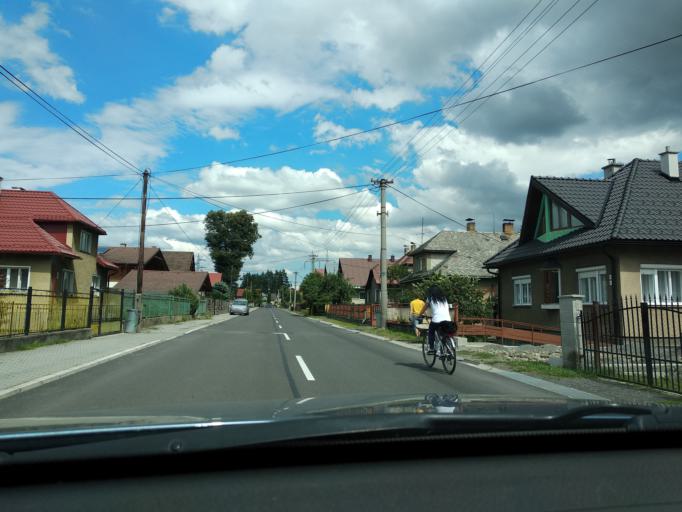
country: SK
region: Zilinsky
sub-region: Okres Zilina
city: Liptovsky Hradok
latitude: 49.0465
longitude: 19.7397
